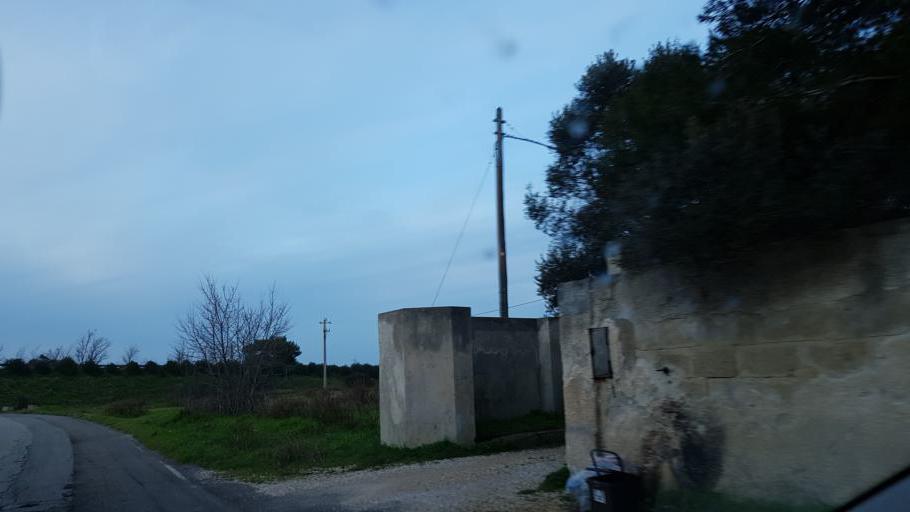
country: IT
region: Apulia
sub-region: Provincia di Brindisi
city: Brindisi
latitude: 40.6583
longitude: 17.9117
